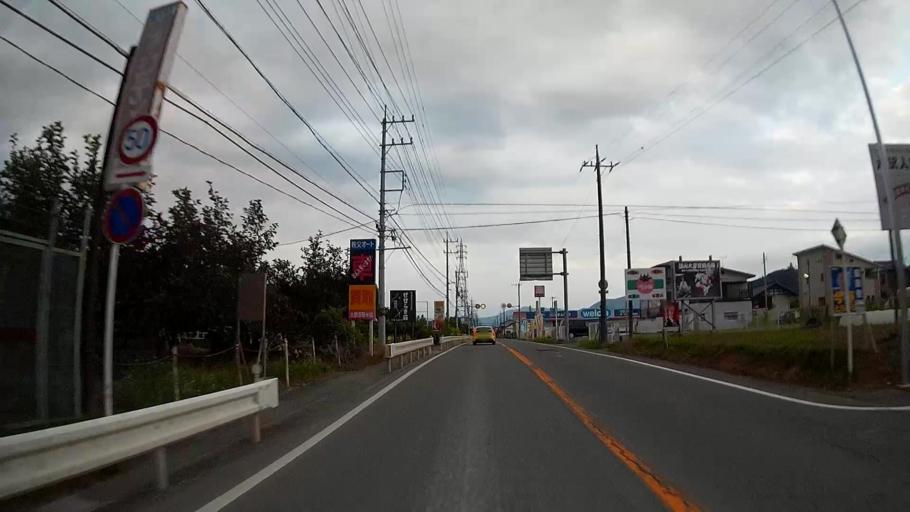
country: JP
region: Saitama
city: Chichibu
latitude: 35.9695
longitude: 139.0621
